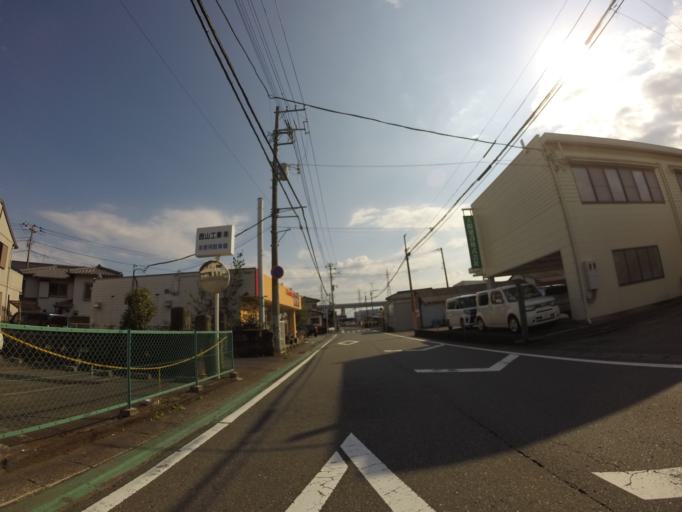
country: JP
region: Shizuoka
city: Fujinomiya
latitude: 35.2009
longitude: 138.6372
